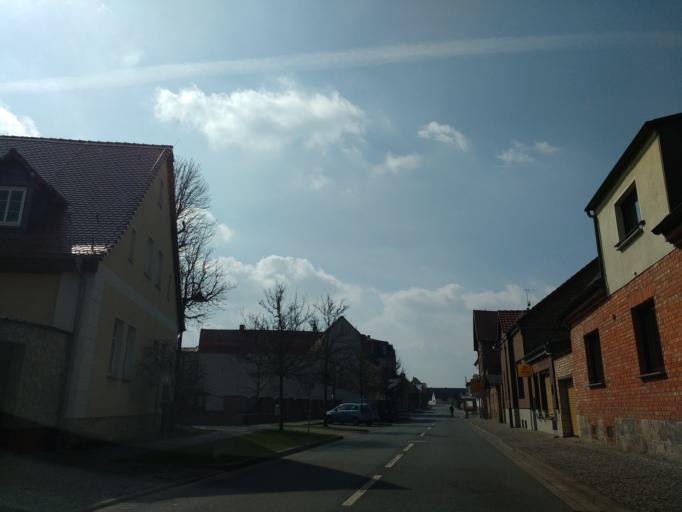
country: DE
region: Saxony-Anhalt
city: Roblingen am See
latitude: 51.4636
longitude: 11.6728
